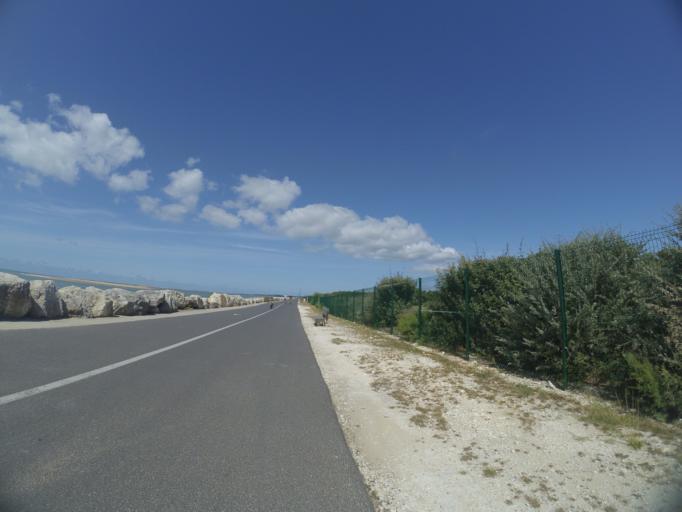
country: FR
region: Poitou-Charentes
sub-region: Departement de la Charente-Maritime
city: Les Mathes
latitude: 45.6753
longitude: -1.1659
